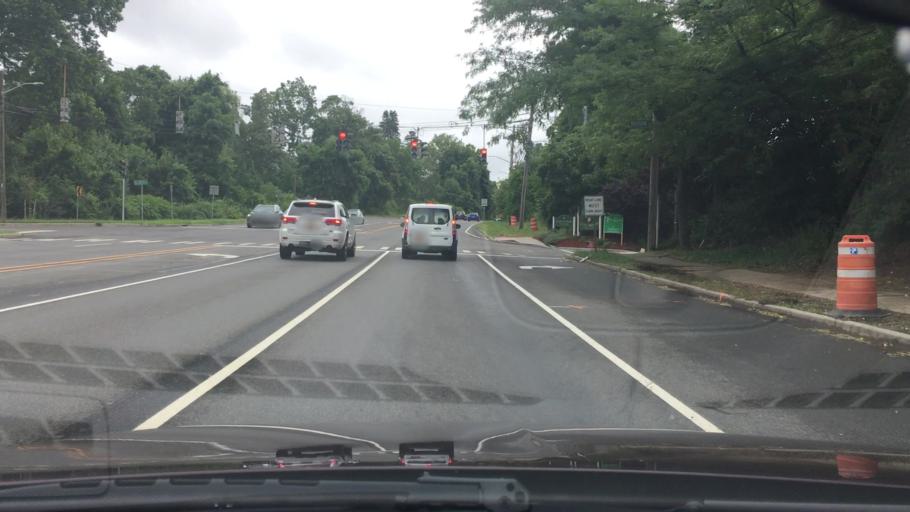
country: US
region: New York
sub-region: Nassau County
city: Jericho
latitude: 40.7974
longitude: -73.5335
